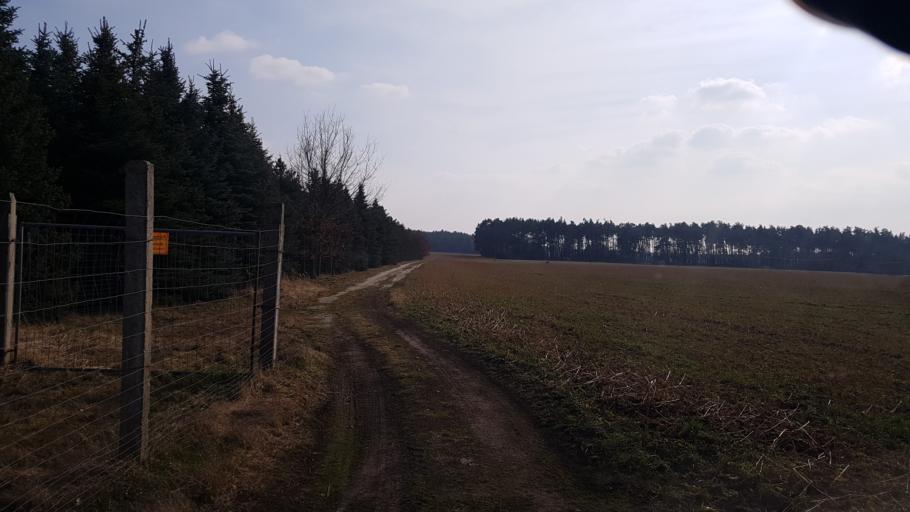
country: DE
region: Brandenburg
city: Schilda
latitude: 51.6367
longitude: 13.3792
